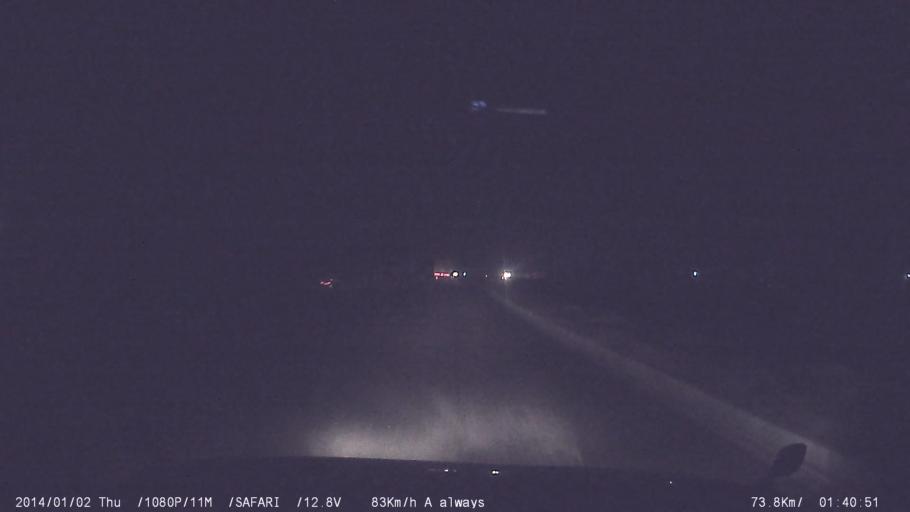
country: IN
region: Tamil Nadu
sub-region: Tiruppur
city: Avinashi
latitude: 11.1573
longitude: 77.2178
